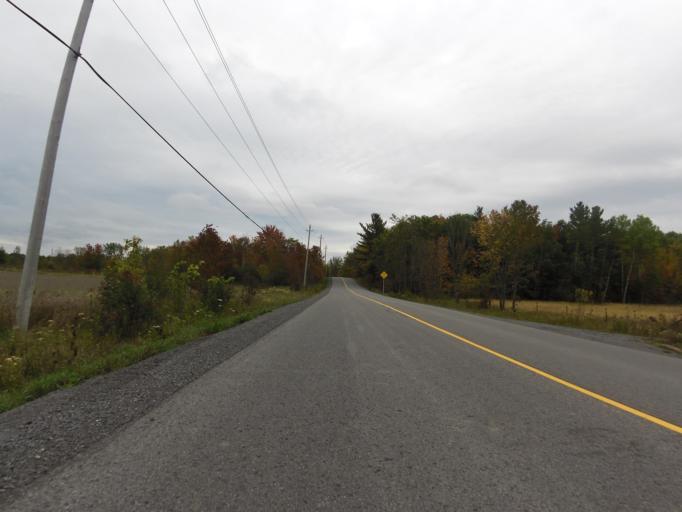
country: CA
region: Ontario
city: Arnprior
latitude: 45.4184
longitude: -76.0904
